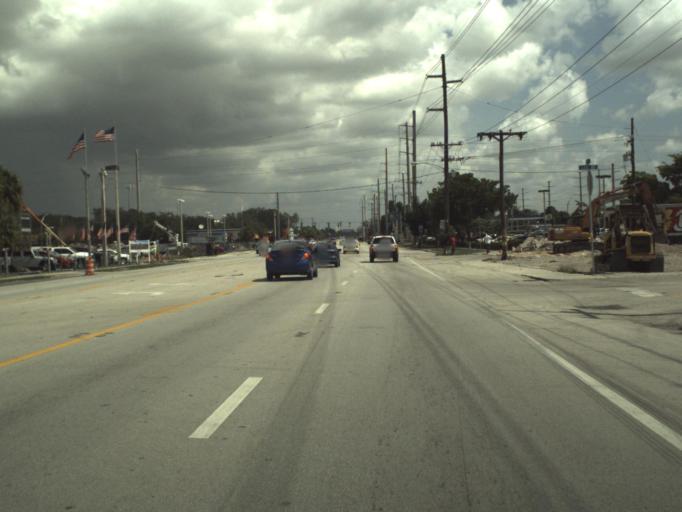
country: US
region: Florida
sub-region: Broward County
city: Pembroke Pines
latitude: 26.0295
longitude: -80.2082
